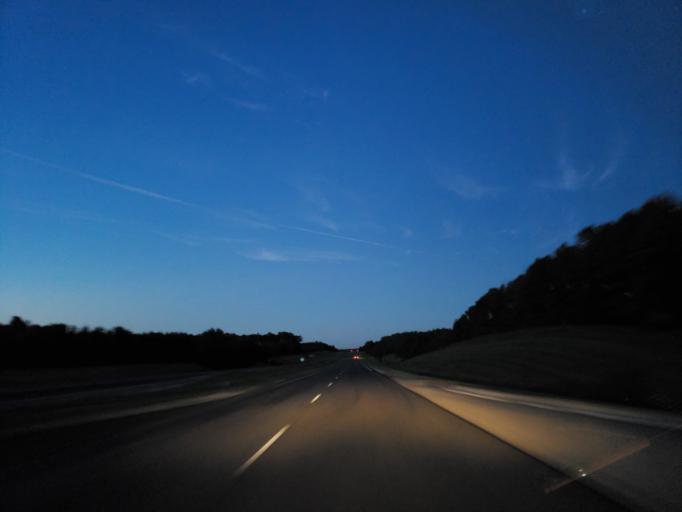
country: US
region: Mississippi
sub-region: Clarke County
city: Quitman
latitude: 32.0127
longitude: -88.6878
